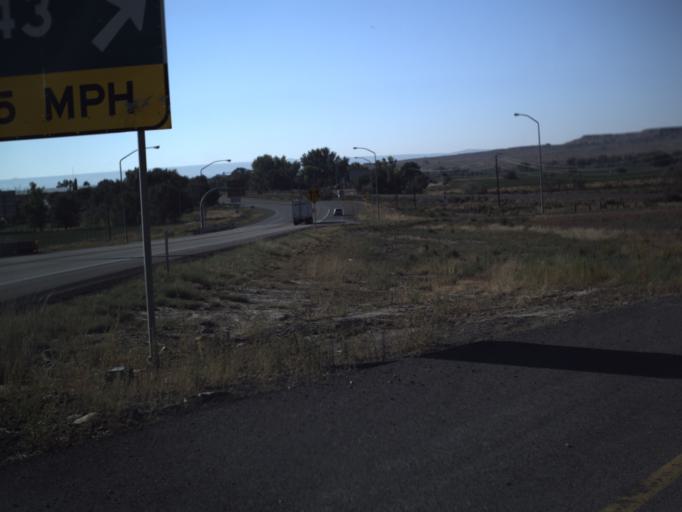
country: US
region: Utah
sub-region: Carbon County
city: Price
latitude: 39.5856
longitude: -110.7882
